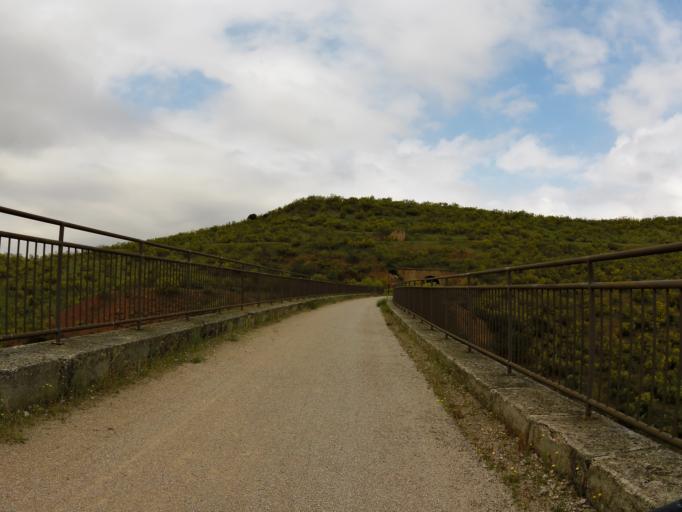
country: ES
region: Castille-La Mancha
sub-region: Provincia de Albacete
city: Alcaraz
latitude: 38.7008
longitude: -2.4971
